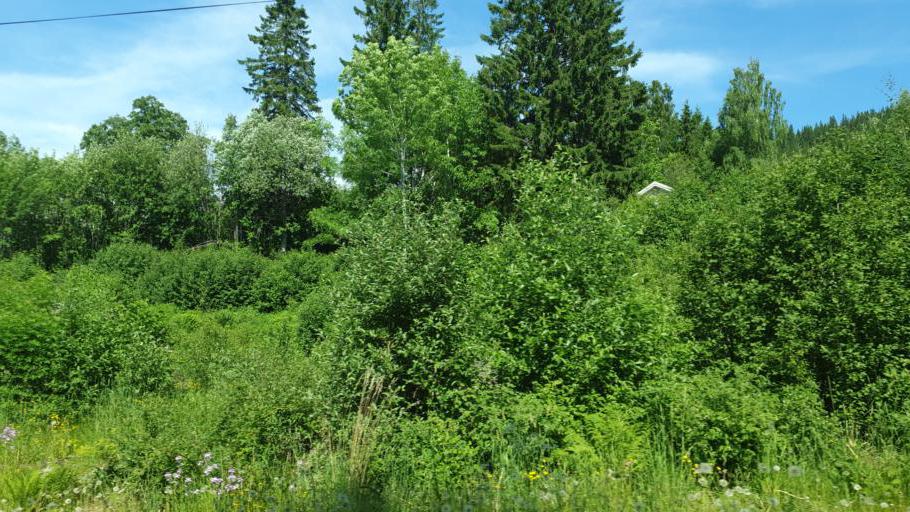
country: NO
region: Nord-Trondelag
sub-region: Leksvik
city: Leksvik
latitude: 63.6791
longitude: 10.6571
